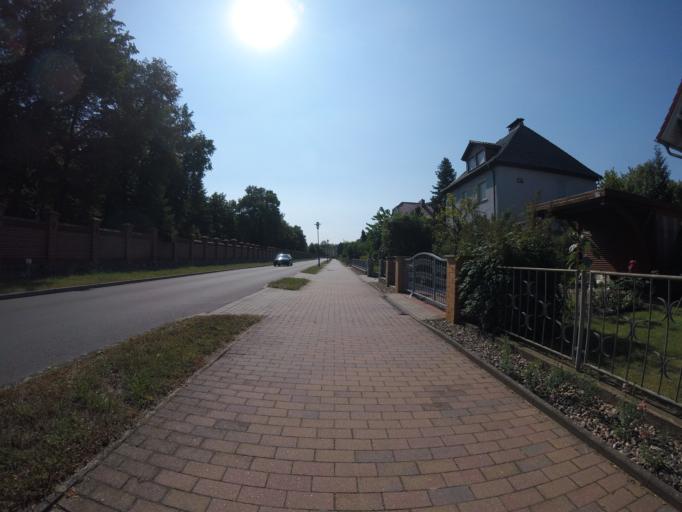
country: DE
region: Brandenburg
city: Mullrose
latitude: 52.2447
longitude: 14.4092
